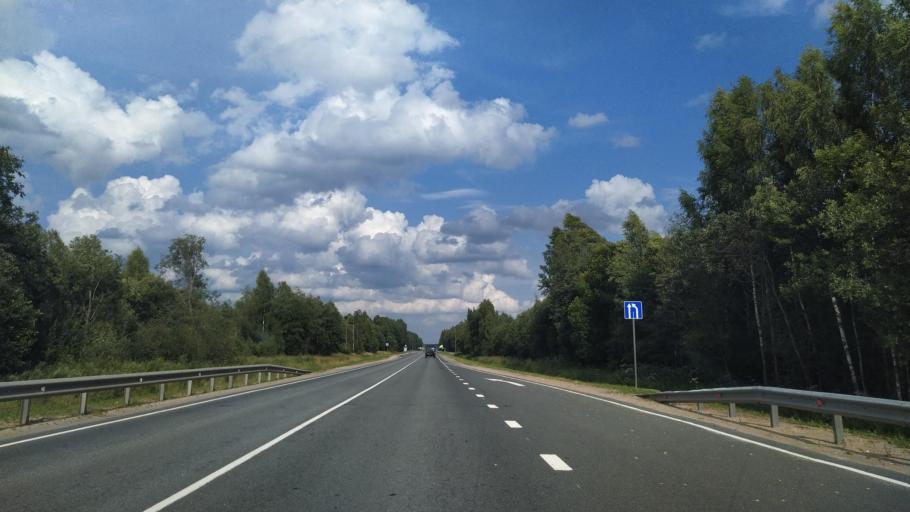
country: RU
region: Novgorod
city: Sol'tsy
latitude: 58.1695
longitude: 30.4874
